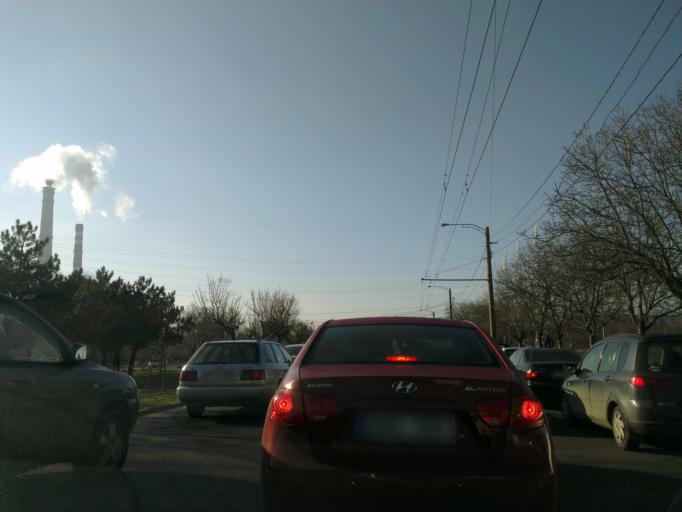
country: MD
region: Chisinau
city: Chisinau
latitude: 47.0352
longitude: 28.8890
